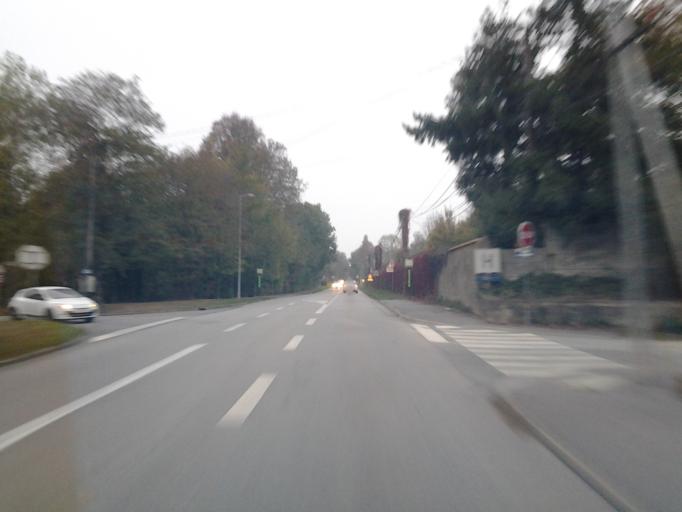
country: FR
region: Pays de la Loire
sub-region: Departement de la Vendee
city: La Roche-sur-Yon
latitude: 46.6443
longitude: -1.4258
